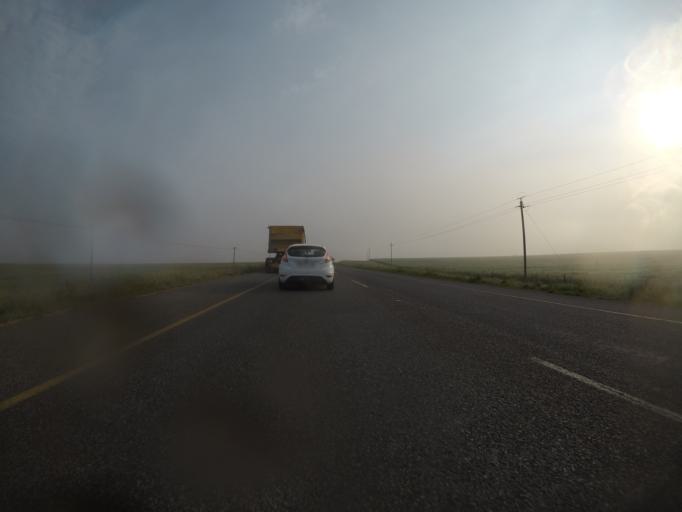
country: ZA
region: Western Cape
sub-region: City of Cape Town
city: Kraaifontein
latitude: -33.6581
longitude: 18.7083
